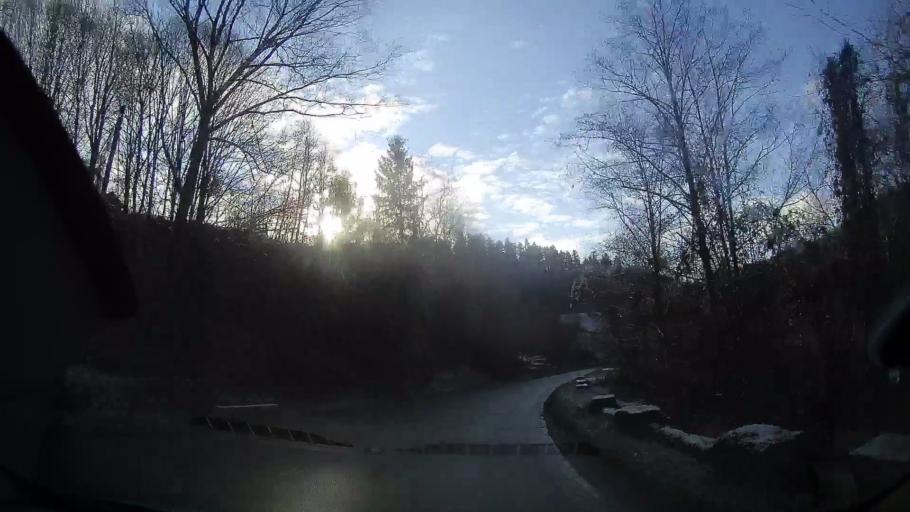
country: RO
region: Alba
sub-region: Comuna Sohodol
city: Sohodol
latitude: 46.3665
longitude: 23.0293
